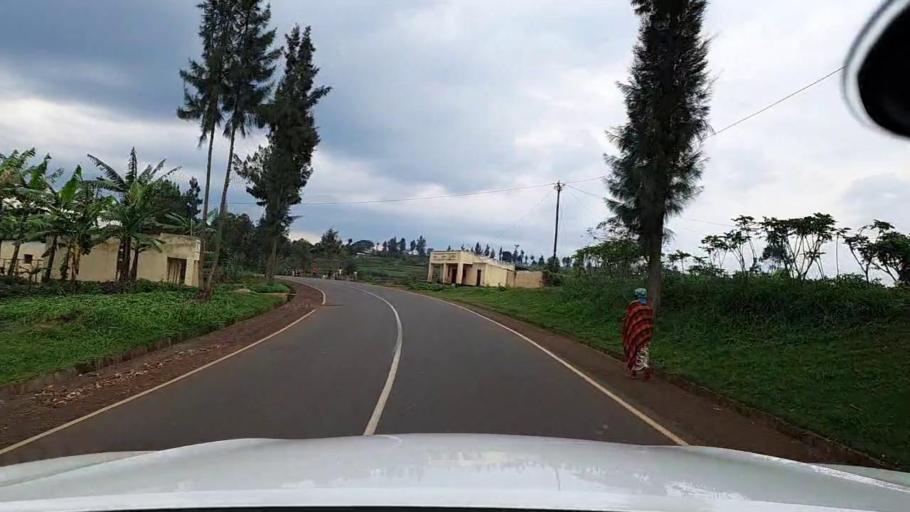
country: RW
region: Western Province
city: Cyangugu
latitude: -2.5941
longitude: 28.9265
